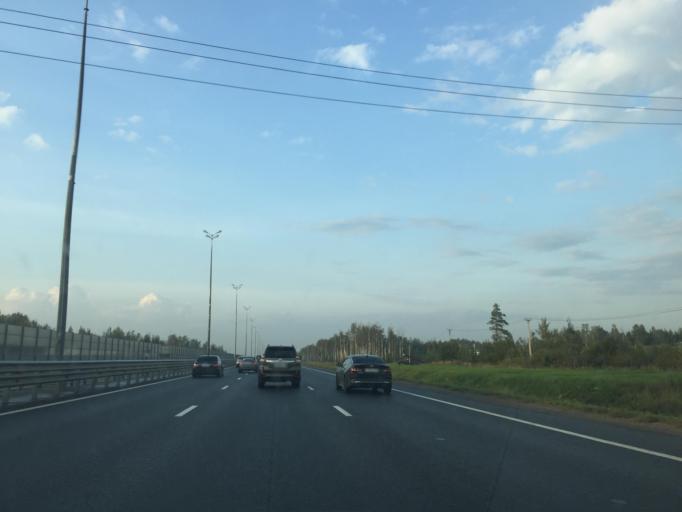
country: RU
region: Leningrad
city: Gatchina
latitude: 59.5629
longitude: 30.1670
